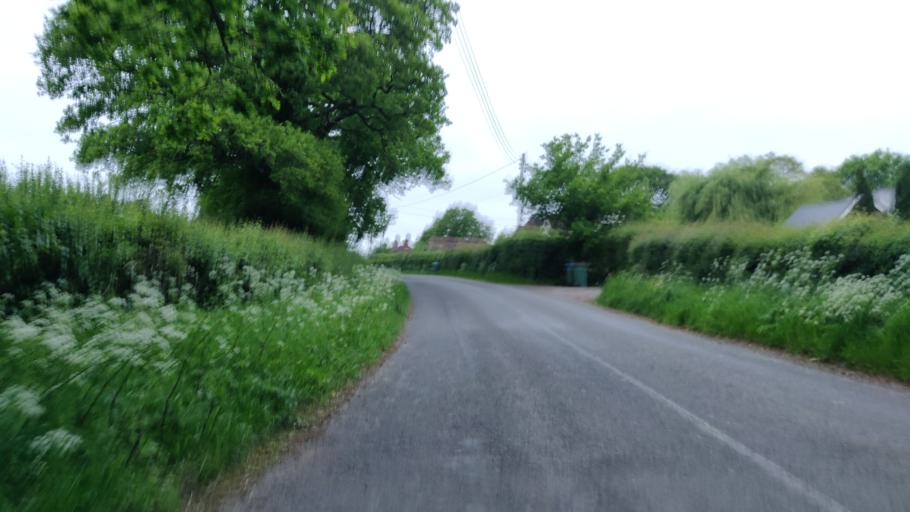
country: GB
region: England
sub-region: West Sussex
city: Partridge Green
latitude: 50.9965
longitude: -0.3026
